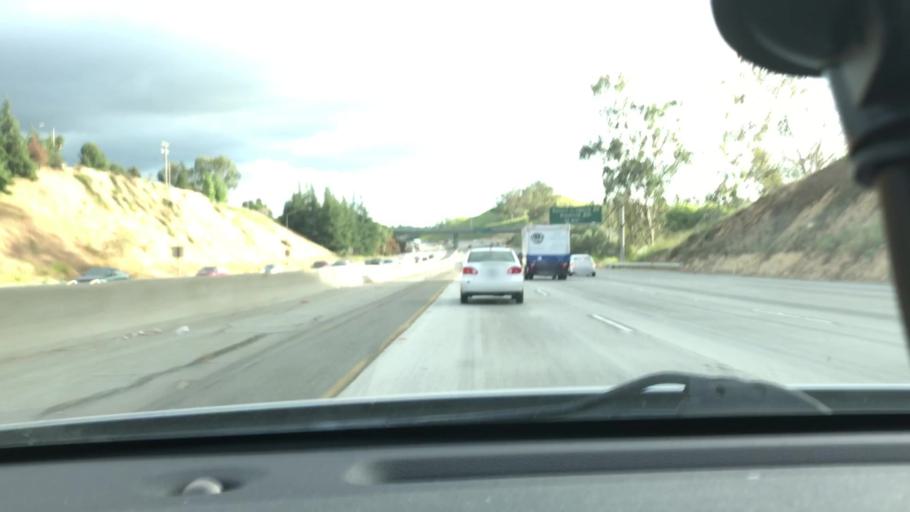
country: US
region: California
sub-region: Los Angeles County
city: Diamond Bar
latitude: 34.0399
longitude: -117.8035
